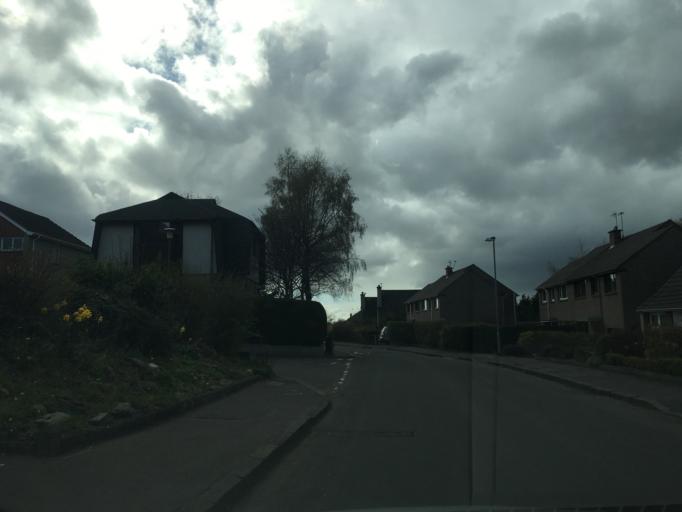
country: GB
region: Scotland
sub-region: Edinburgh
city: Edinburgh
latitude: 55.9093
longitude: -3.2032
